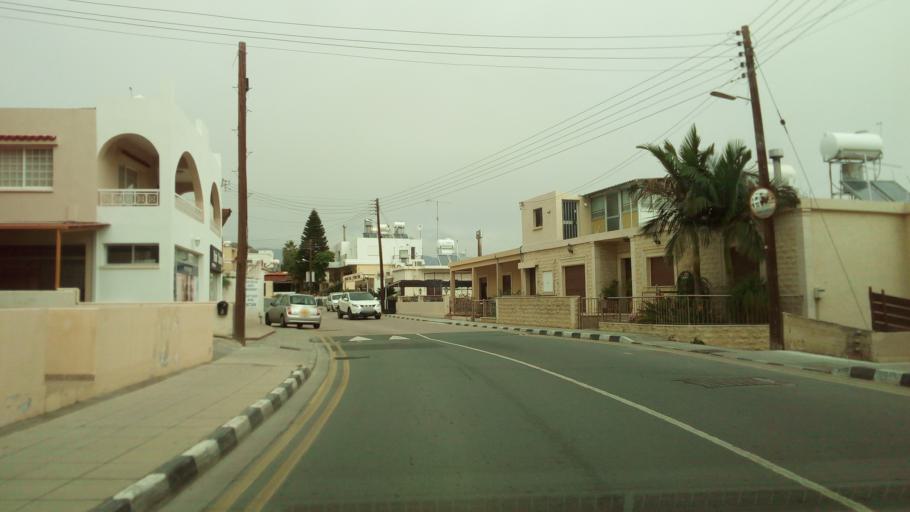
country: CY
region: Limassol
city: Mouttagiaka
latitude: 34.7165
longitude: 33.0861
